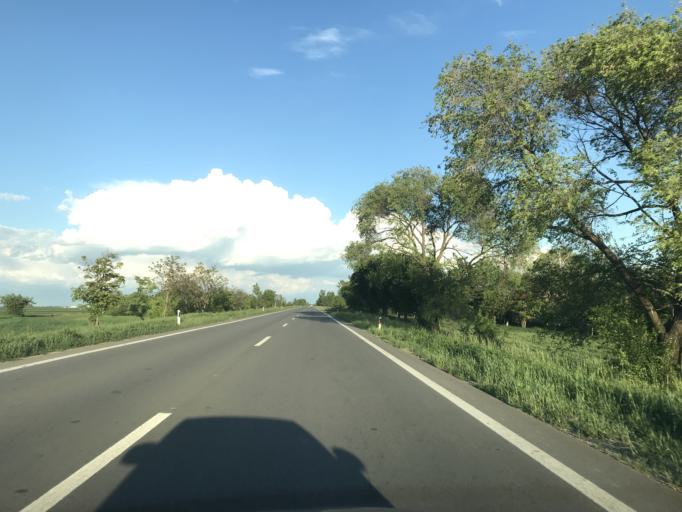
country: RS
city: Aradac
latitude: 45.3896
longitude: 20.3066
